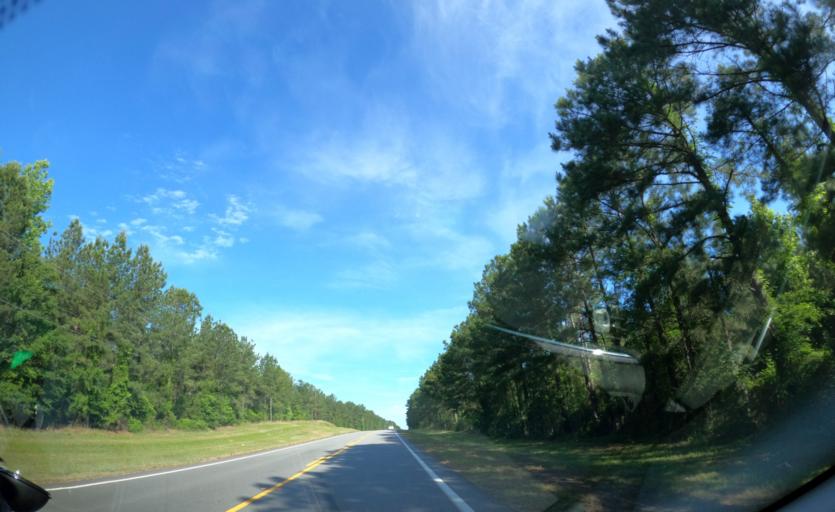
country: US
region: Georgia
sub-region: Columbia County
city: Appling
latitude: 33.6282
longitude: -82.2887
